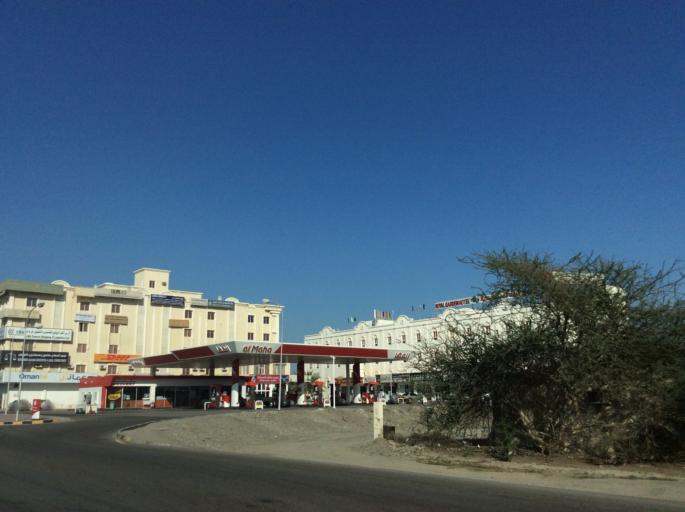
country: OM
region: Al Batinah
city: Al Liwa'
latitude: 24.4388
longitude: 56.6082
